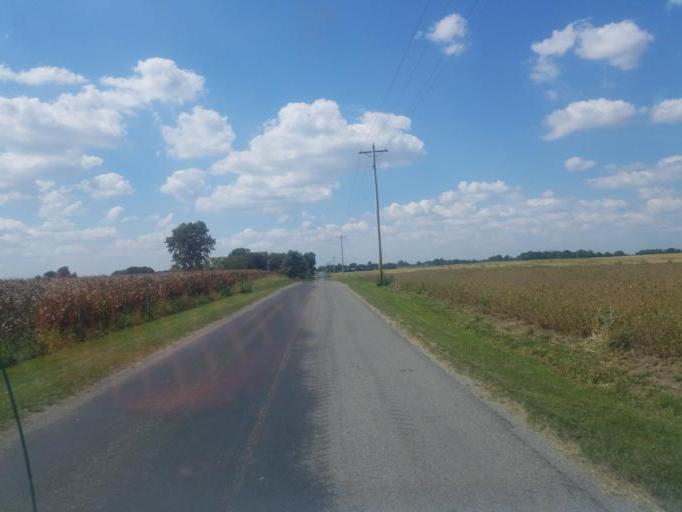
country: US
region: Ohio
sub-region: Hardin County
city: Ada
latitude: 40.6524
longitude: -83.8734
